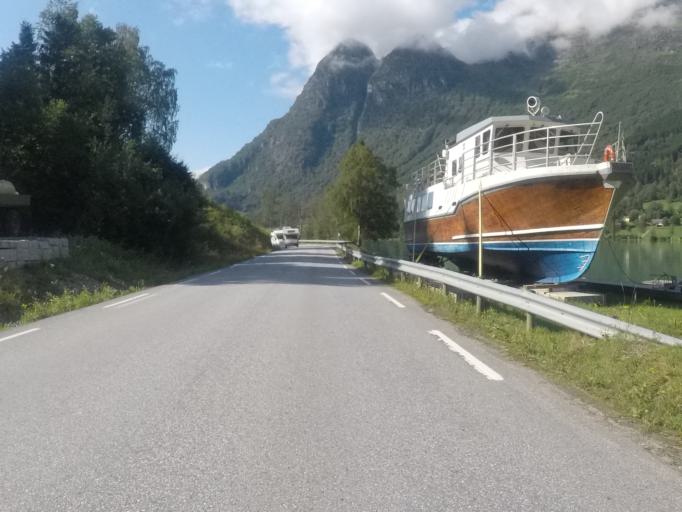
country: NO
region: Sogn og Fjordane
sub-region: Stryn
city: Stryn
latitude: 61.7975
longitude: 6.8280
